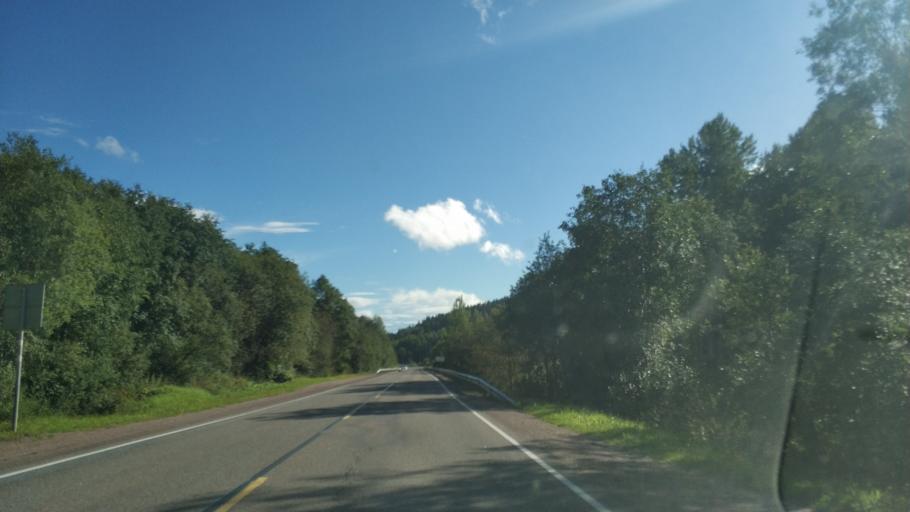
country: RU
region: Republic of Karelia
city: Sortavala
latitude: 61.6710
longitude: 30.6541
